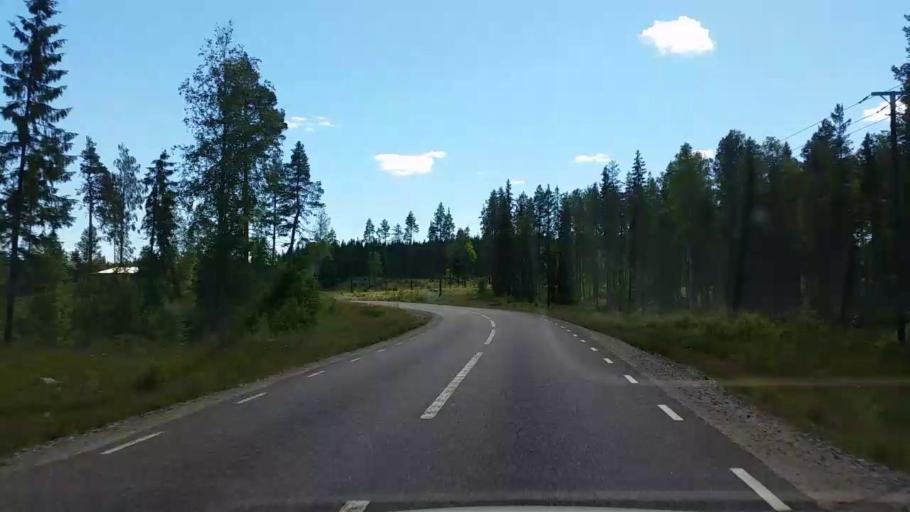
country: SE
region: Gaevleborg
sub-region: Ovanakers Kommun
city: Edsbyn
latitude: 61.5309
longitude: 15.6785
